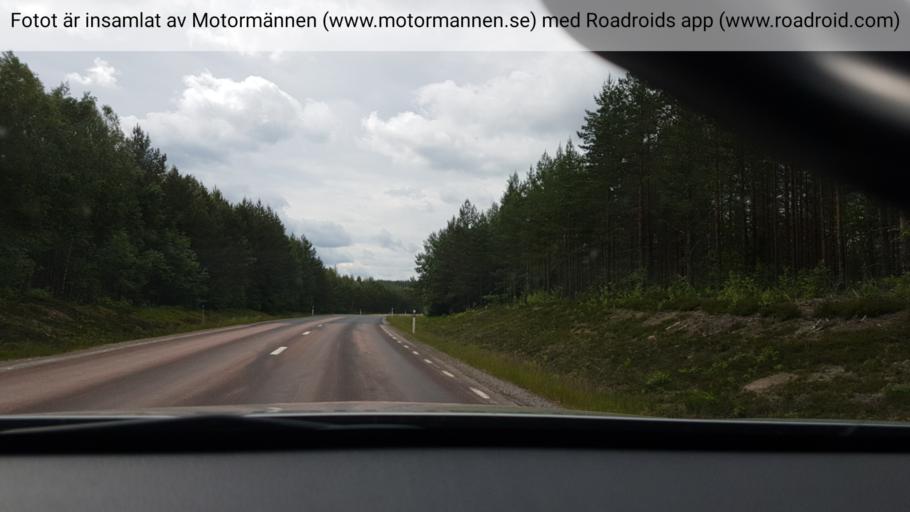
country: SE
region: Vaermland
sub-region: Hagfors Kommun
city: Ekshaerad
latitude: 60.3898
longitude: 13.2605
